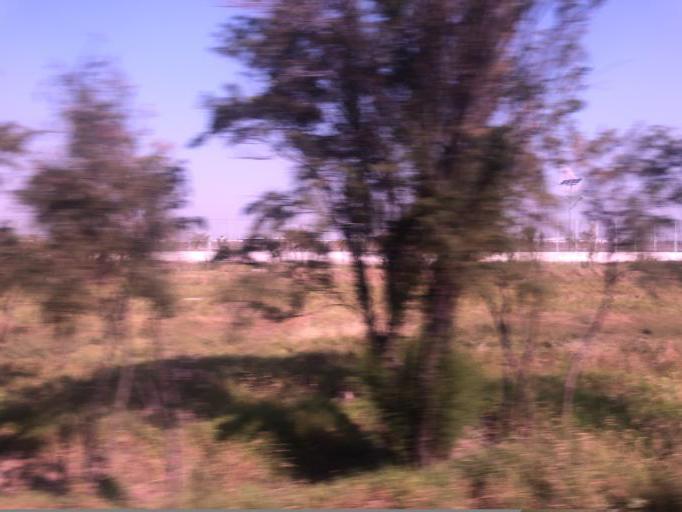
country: MX
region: Mexico
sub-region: Texcoco
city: Colonia Guadalupe Victoria
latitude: 19.4789
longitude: -98.9789
